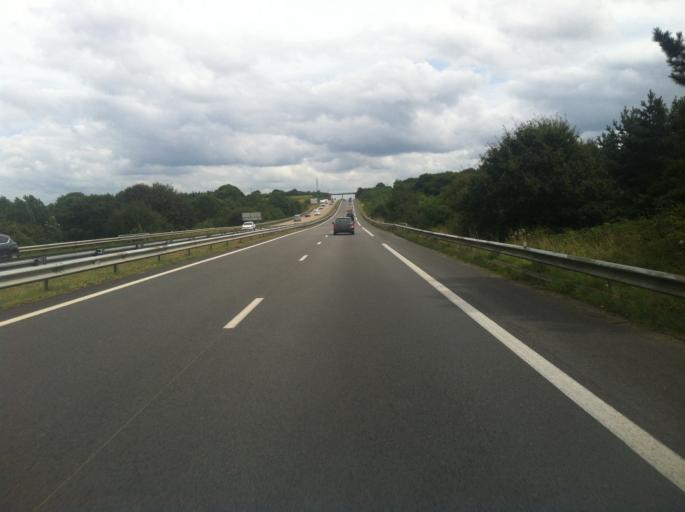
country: FR
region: Brittany
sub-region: Departement du Finistere
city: Guerlesquin
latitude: 48.5688
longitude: -3.5967
